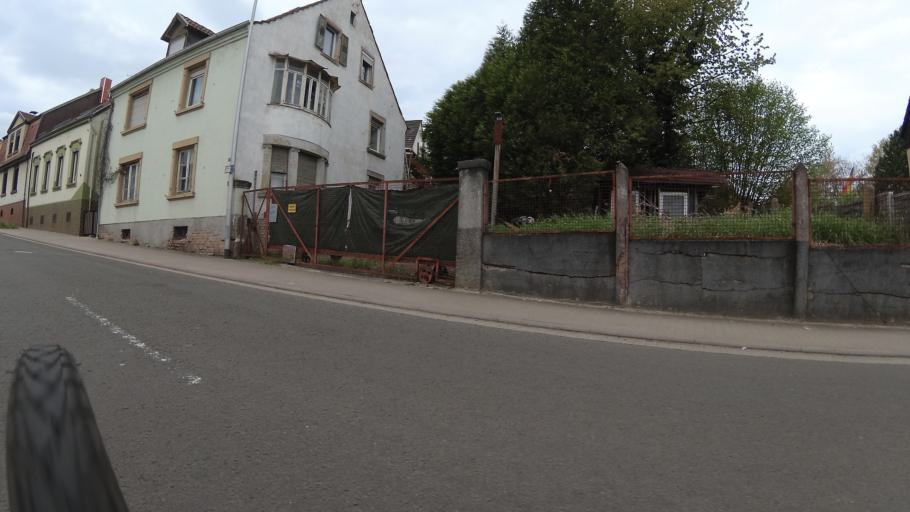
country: DE
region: Rheinland-Pfalz
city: Zweibrucken
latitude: 49.2449
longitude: 7.3499
